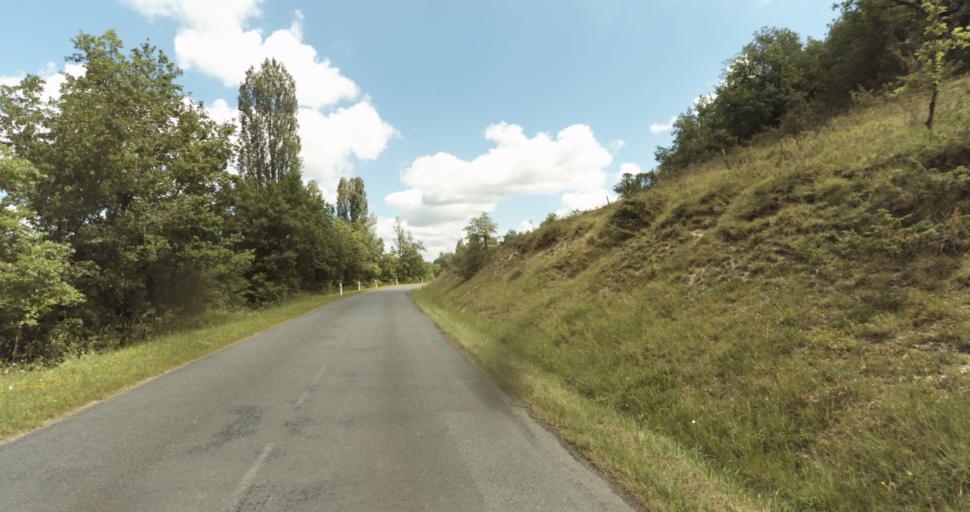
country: FR
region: Aquitaine
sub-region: Departement de la Dordogne
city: Beaumont-du-Perigord
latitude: 44.7606
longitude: 0.7347
